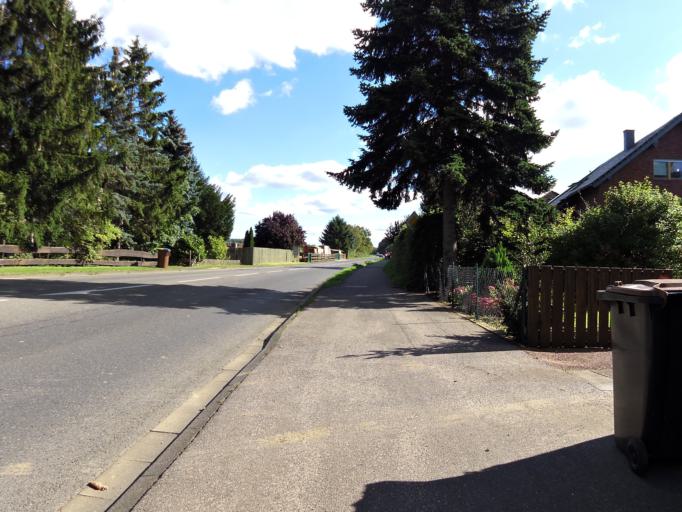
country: DE
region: North Rhine-Westphalia
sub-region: Regierungsbezirk Koln
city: Euskirchen
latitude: 50.6292
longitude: 6.8163
